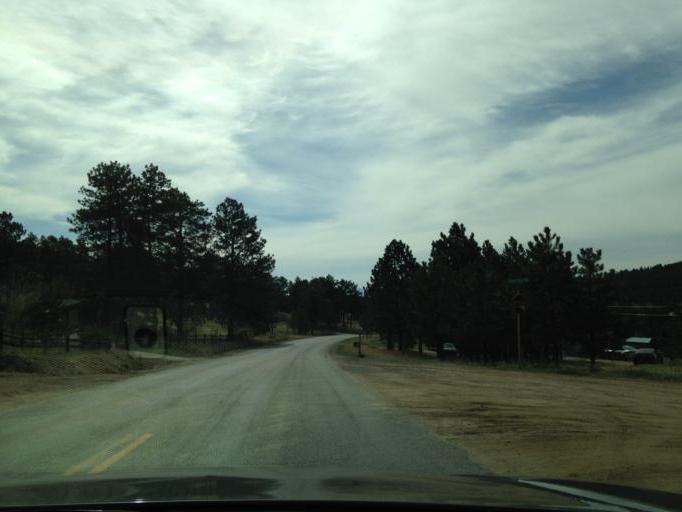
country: US
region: Colorado
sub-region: Jefferson County
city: Evergreen
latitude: 39.4269
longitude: -105.4491
